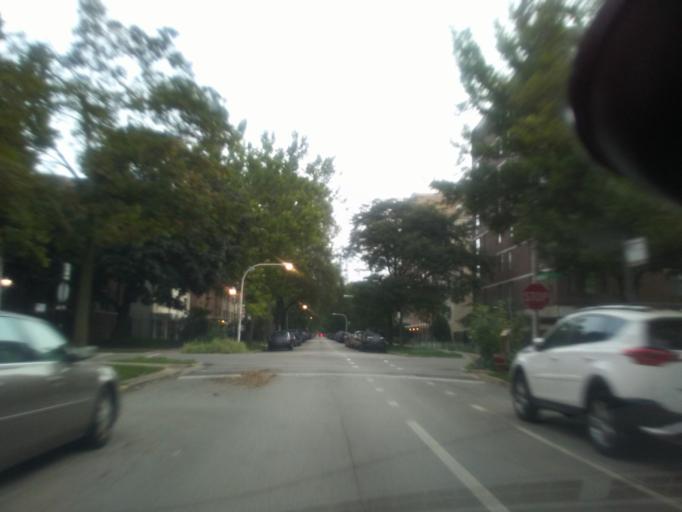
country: US
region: Illinois
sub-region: Cook County
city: Evanston
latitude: 41.9899
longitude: -87.6568
